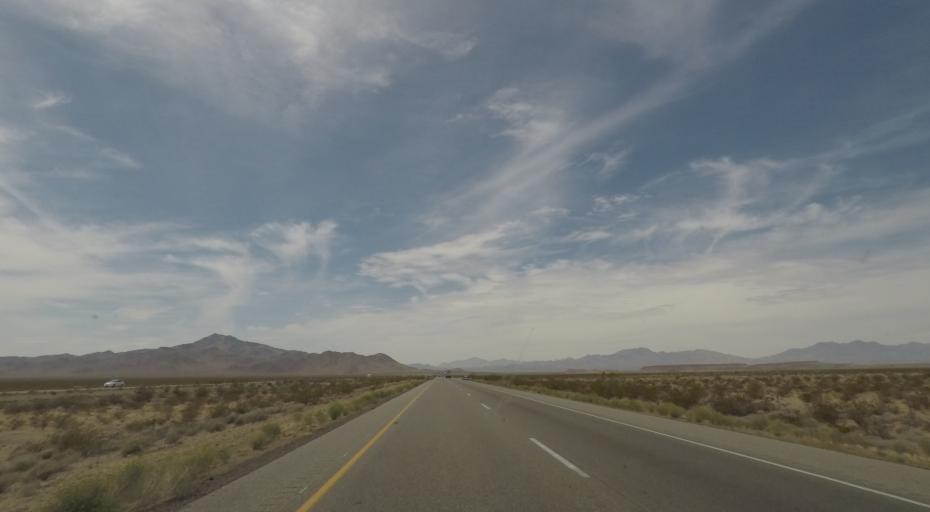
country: US
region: California
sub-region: San Bernardino County
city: Needles
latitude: 34.8049
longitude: -115.2749
